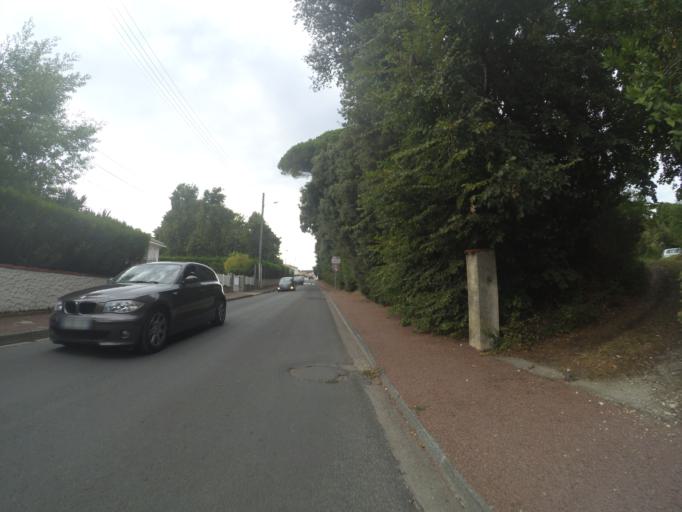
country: FR
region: Poitou-Charentes
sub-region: Departement de la Charente-Maritime
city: Meschers-sur-Gironde
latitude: 45.5600
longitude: -0.9572
